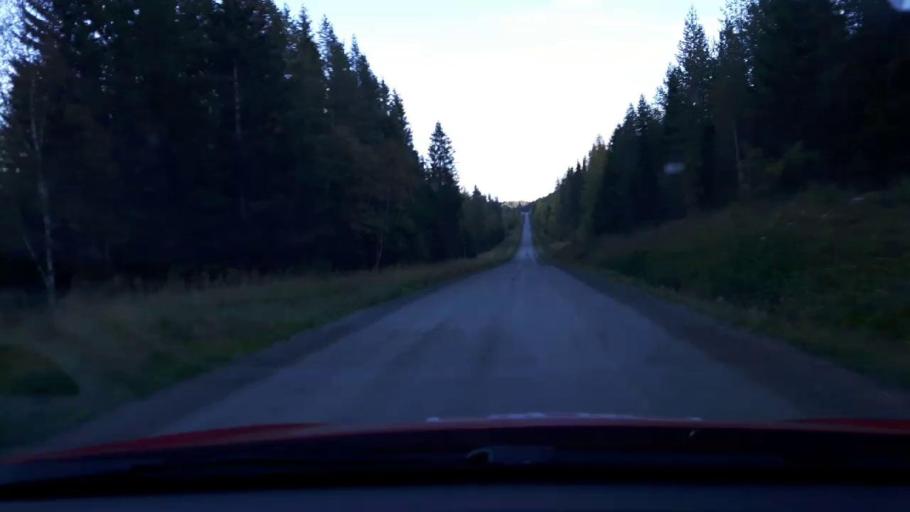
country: SE
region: Jaemtland
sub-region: OEstersunds Kommun
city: Brunflo
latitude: 62.9429
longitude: 14.9874
